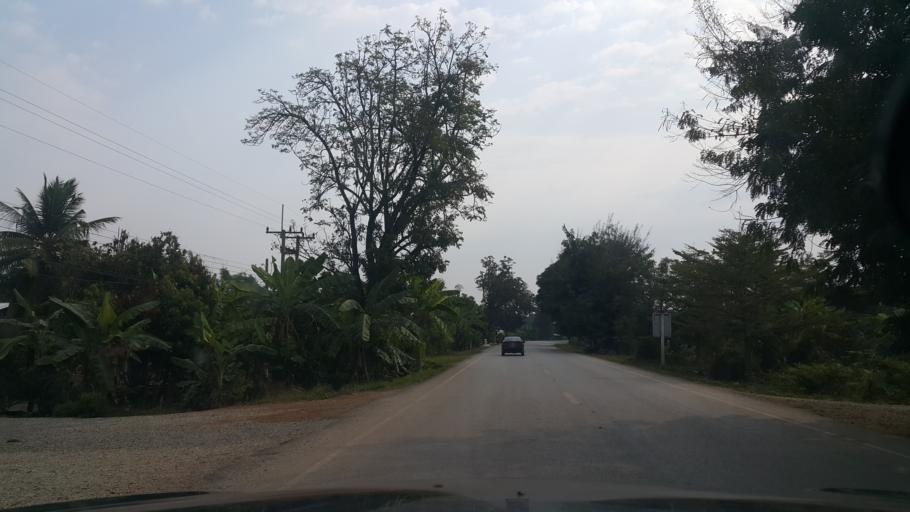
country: TH
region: Sukhothai
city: Si Samrong
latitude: 17.1830
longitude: 99.8302
